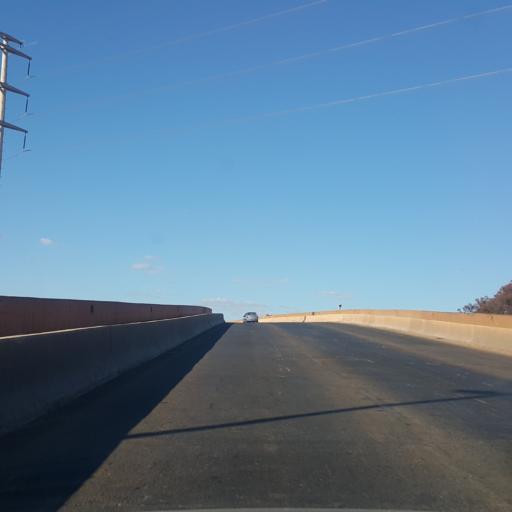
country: BR
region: Federal District
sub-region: Brasilia
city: Brasilia
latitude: -15.7858
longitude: -47.9423
